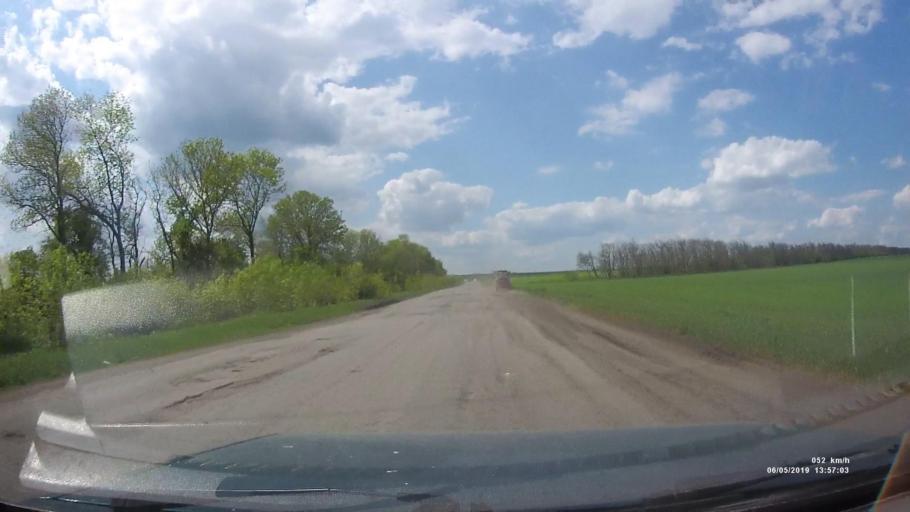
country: RU
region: Rostov
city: Melikhovskaya
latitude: 47.6828
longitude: 40.4246
